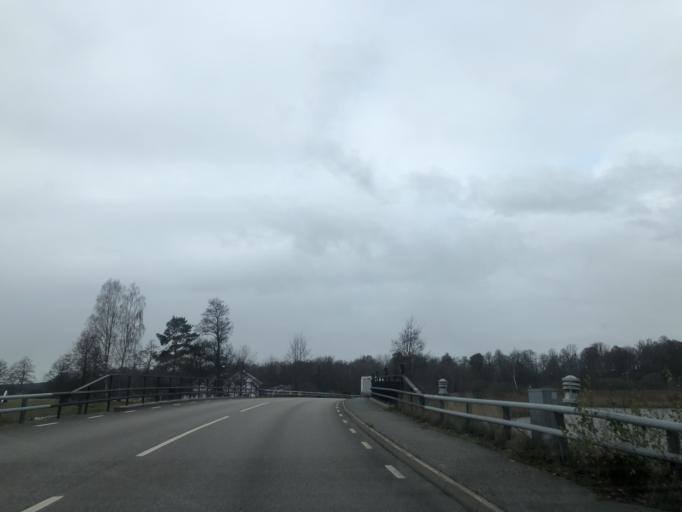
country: SE
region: Vaestra Goetaland
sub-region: Tranemo Kommun
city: Langhem
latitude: 57.6755
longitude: 13.3269
